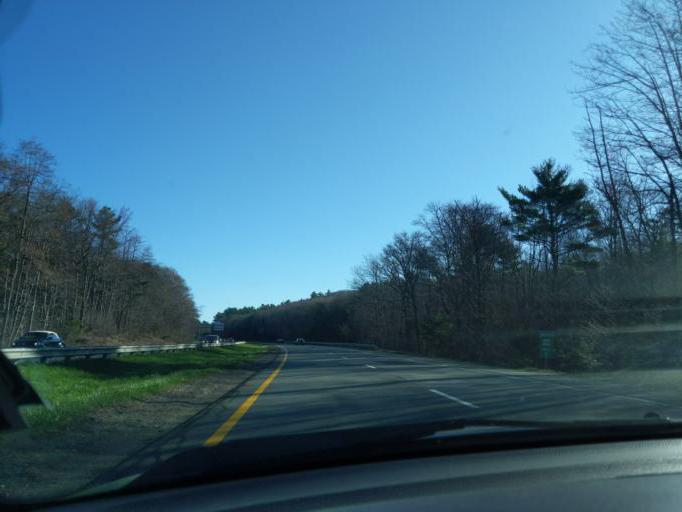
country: US
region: Massachusetts
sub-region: Essex County
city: Essex
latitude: 42.5931
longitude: -70.7547
